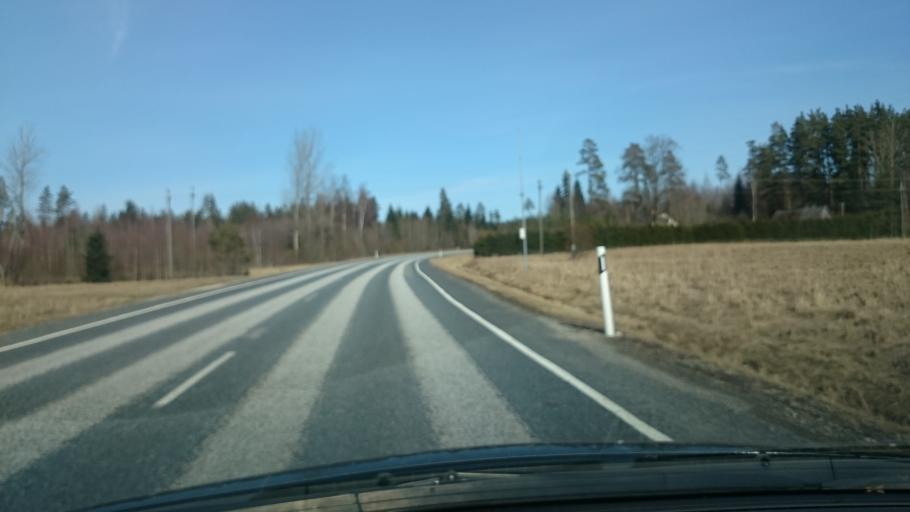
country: EE
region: Jaervamaa
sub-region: Tueri vald
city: Sarevere
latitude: 58.7306
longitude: 25.2874
